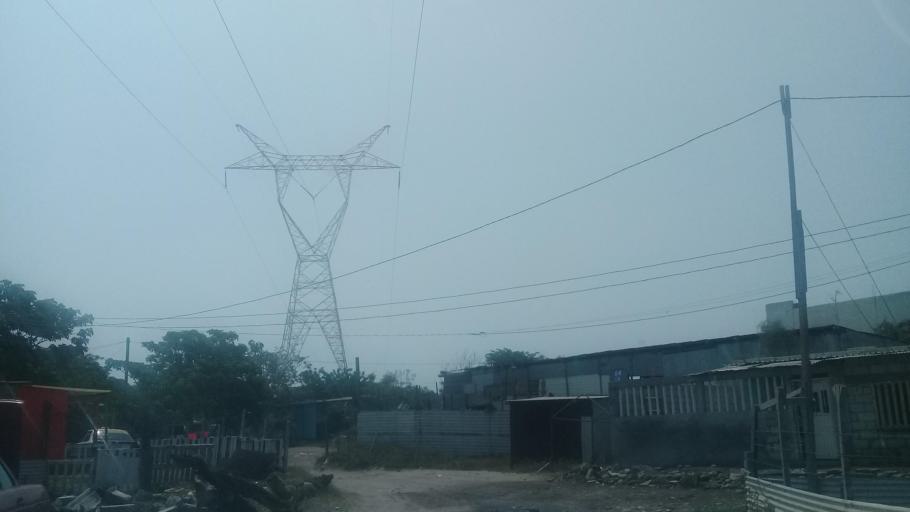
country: MX
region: Veracruz
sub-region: Veracruz
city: Las Amapolas
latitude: 19.1685
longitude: -96.1787
